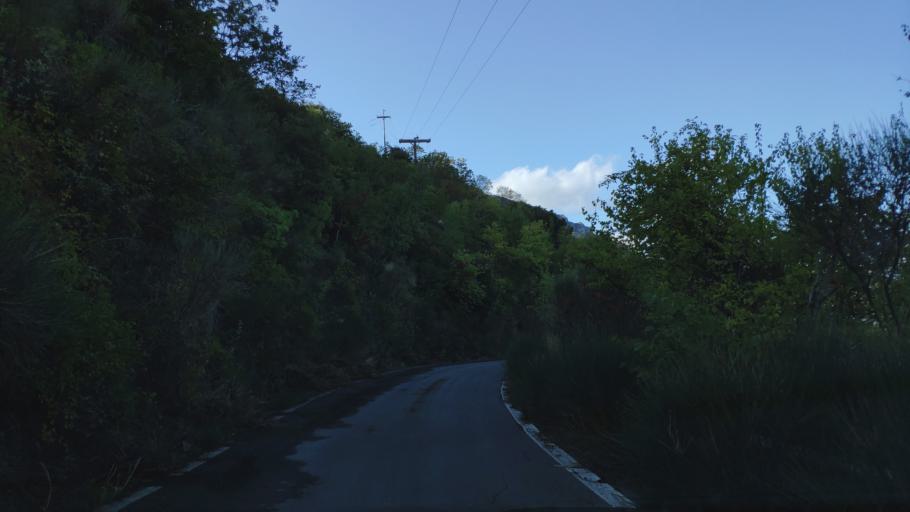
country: GR
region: Peloponnese
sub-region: Nomos Arkadias
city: Dimitsana
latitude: 37.5567
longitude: 22.0403
